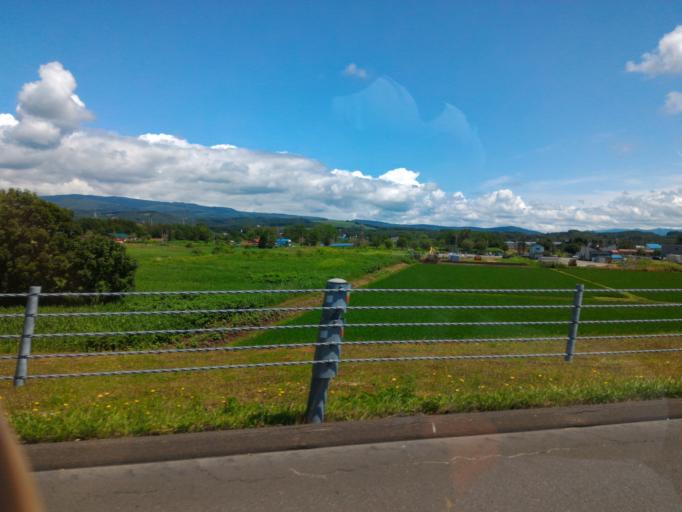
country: JP
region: Hokkaido
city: Nayoro
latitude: 44.3323
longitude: 142.4460
